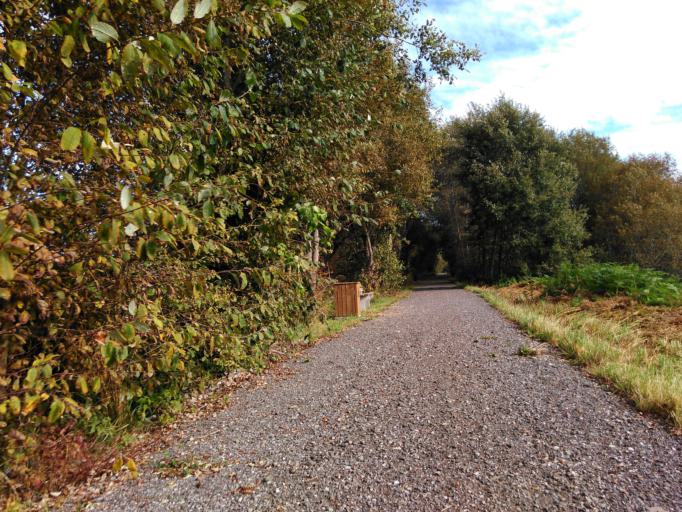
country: BE
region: Wallonia
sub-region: Province du Luxembourg
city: Vaux-sur-Sure
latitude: 49.9242
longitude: 5.5099
